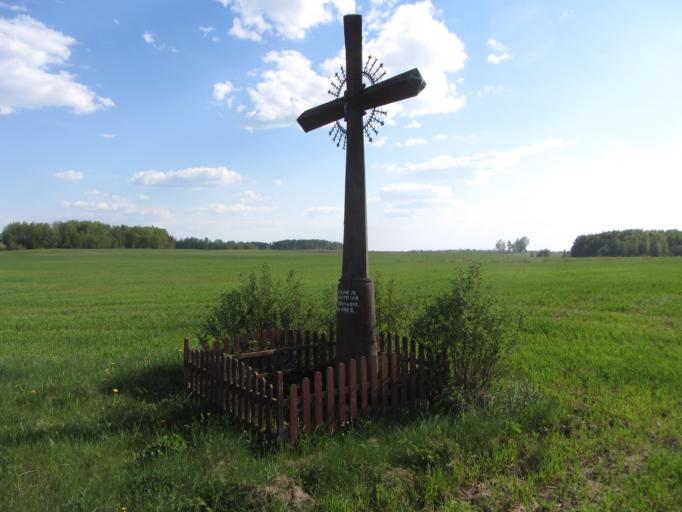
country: LT
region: Utenos apskritis
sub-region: Anyksciai
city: Anyksciai
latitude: 55.3585
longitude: 25.0476
